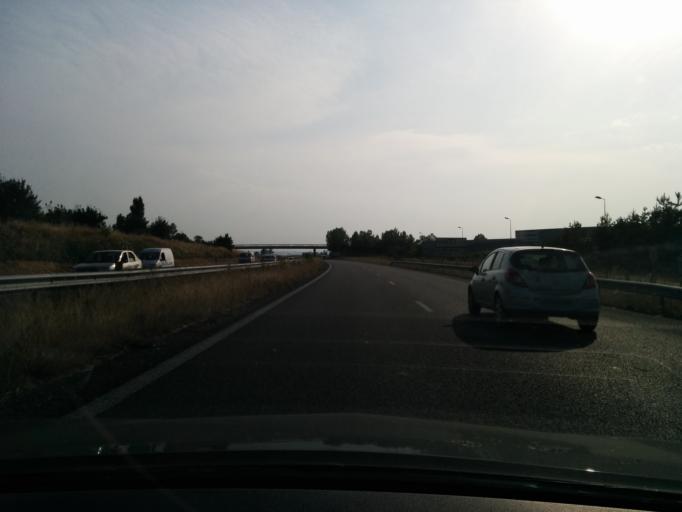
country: FR
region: Midi-Pyrenees
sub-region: Departement du Tarn
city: Coufouleux
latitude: 43.7916
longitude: 1.7497
